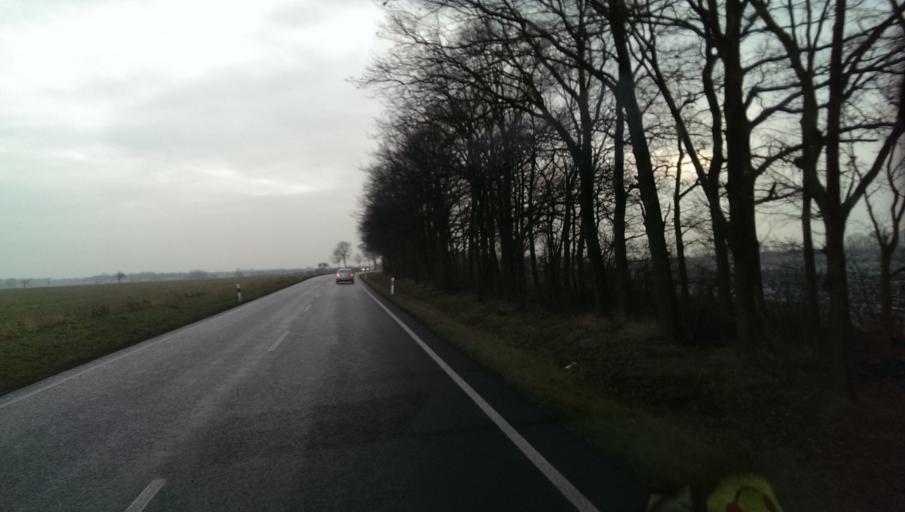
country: DE
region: Saxony
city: Zabeltitz
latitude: 51.3320
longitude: 13.5432
